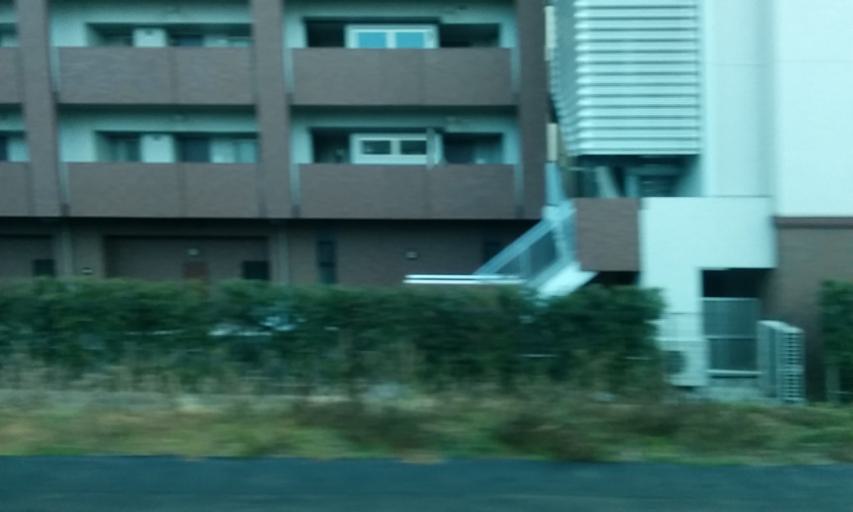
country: JP
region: Saitama
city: Kawaguchi
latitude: 35.7983
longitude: 139.7184
